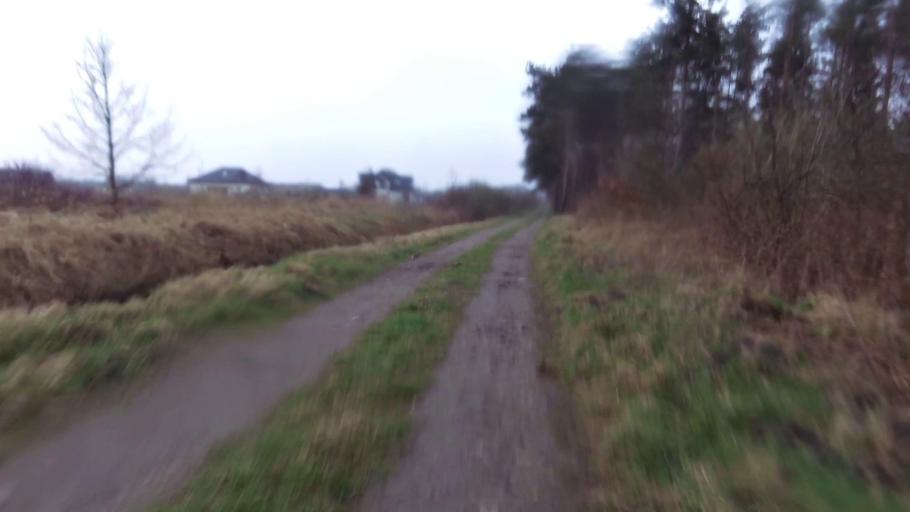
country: PL
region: West Pomeranian Voivodeship
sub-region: Powiat kolobrzeski
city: Grzybowo
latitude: 54.1566
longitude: 15.4992
